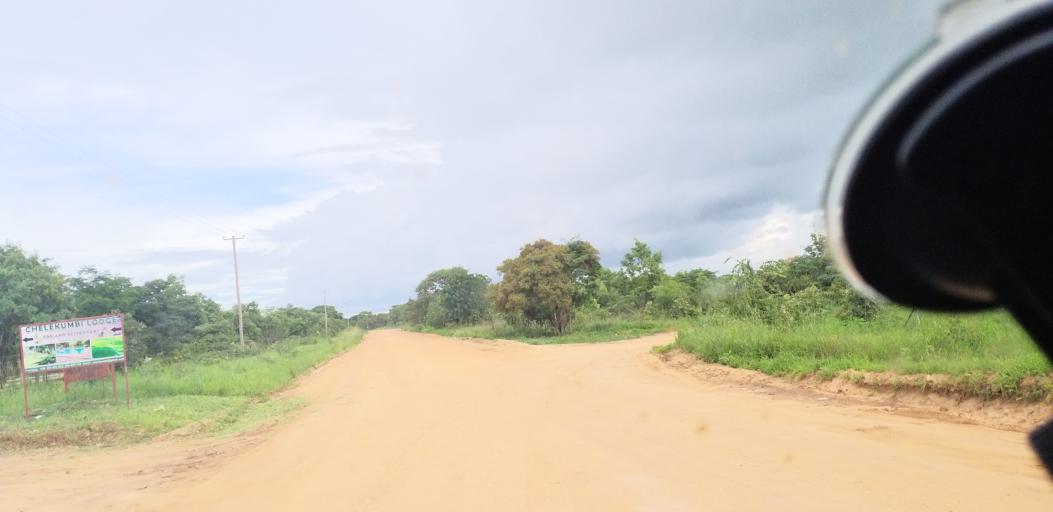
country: ZM
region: Lusaka
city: Chongwe
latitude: -15.1787
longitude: 28.4559
